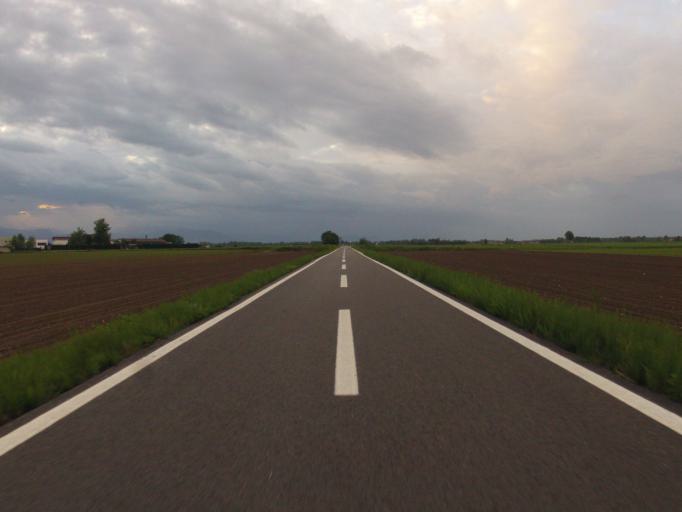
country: IT
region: Piedmont
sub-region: Provincia di Torino
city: Villafranca Piemonte
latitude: 44.7939
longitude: 7.5071
